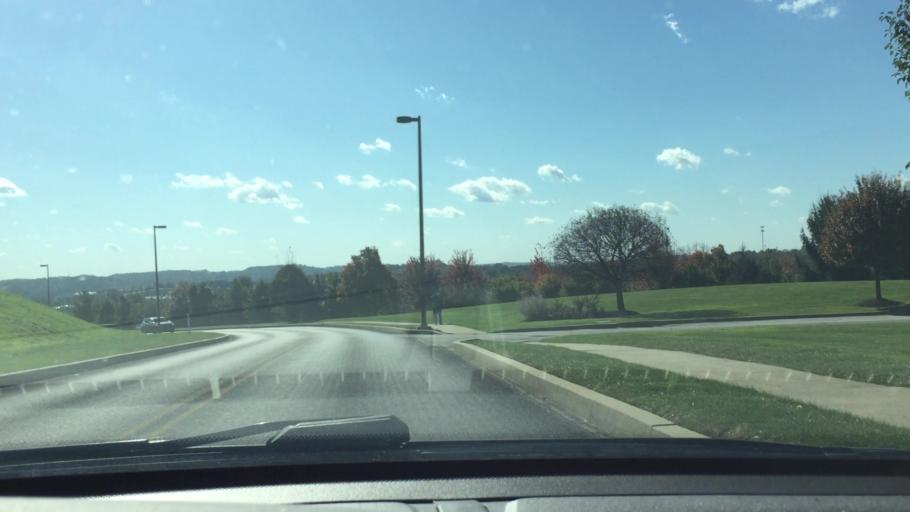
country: US
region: Pennsylvania
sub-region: Washington County
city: Muse
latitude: 40.2991
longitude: -80.1760
